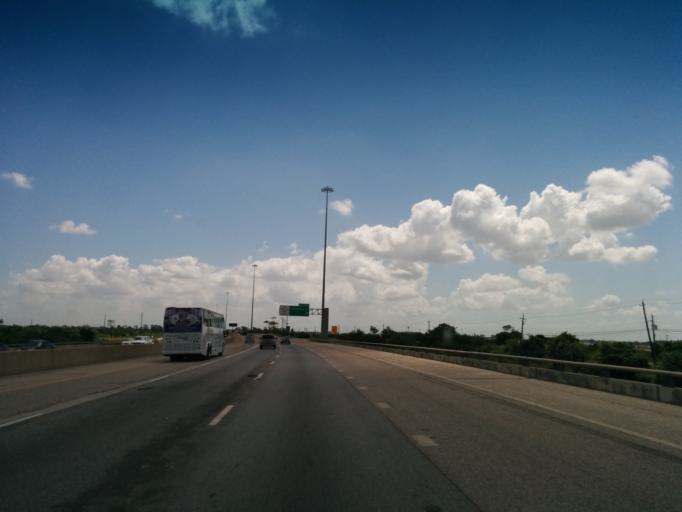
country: US
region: Texas
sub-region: Harris County
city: Channelview
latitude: 29.7910
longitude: -95.0842
